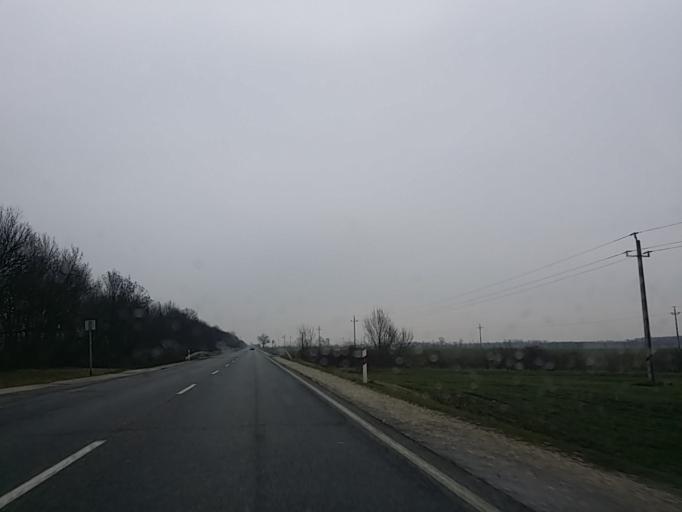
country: HU
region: Borsod-Abauj-Zemplen
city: Mezokovesd
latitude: 47.8282
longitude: 20.6142
